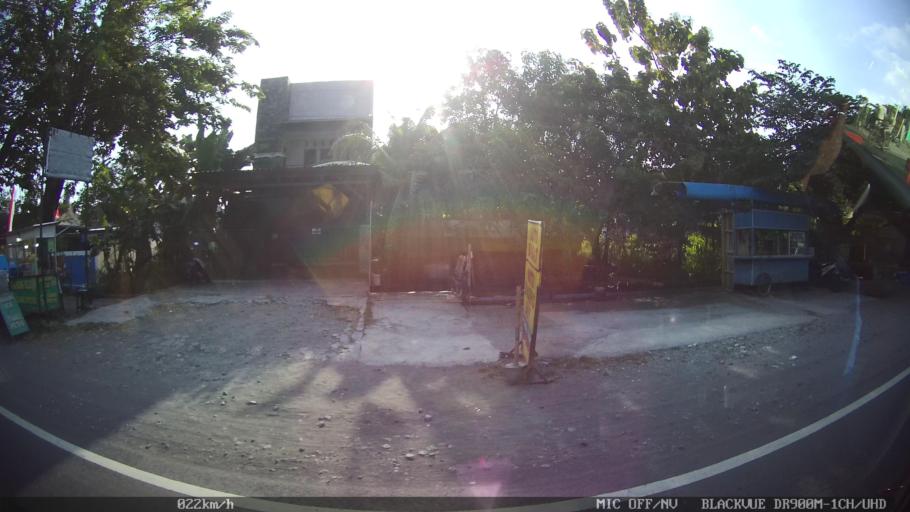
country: ID
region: Daerah Istimewa Yogyakarta
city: Bantul
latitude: -7.8740
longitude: 110.3359
